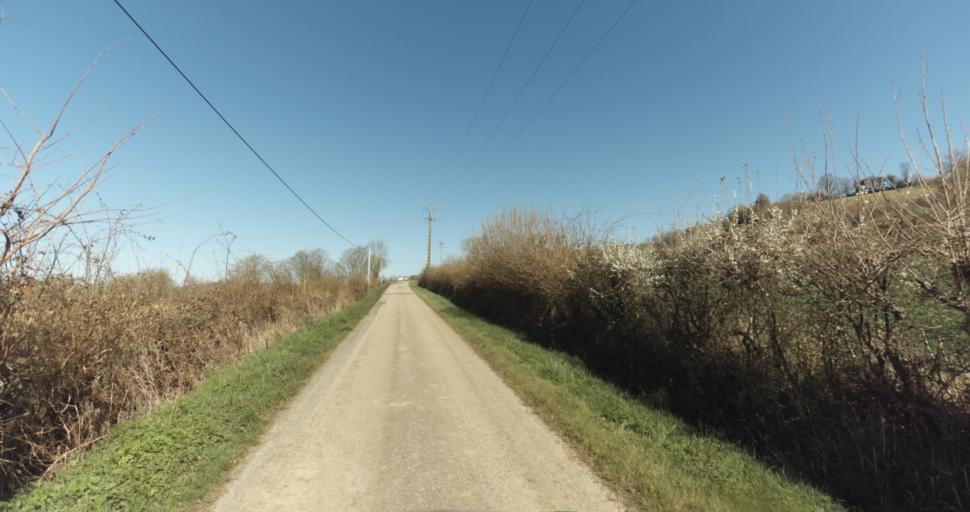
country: FR
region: Lower Normandy
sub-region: Departement du Calvados
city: Livarot
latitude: 48.9628
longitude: 0.0675
